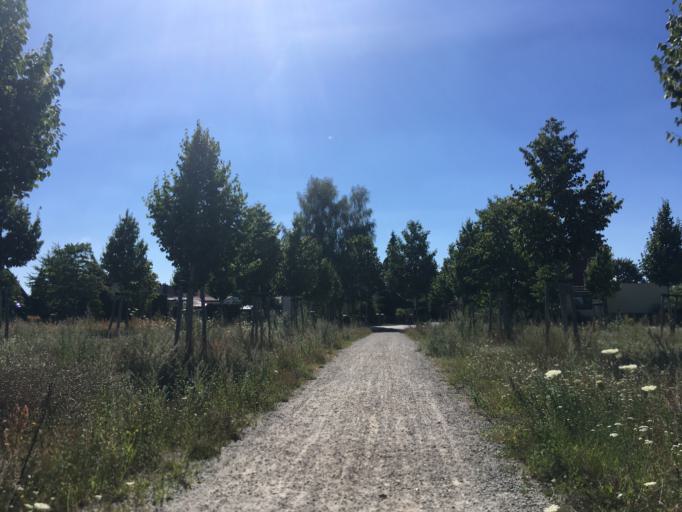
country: DE
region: Brandenburg
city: Altlandsberg
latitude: 52.5374
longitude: 13.7454
